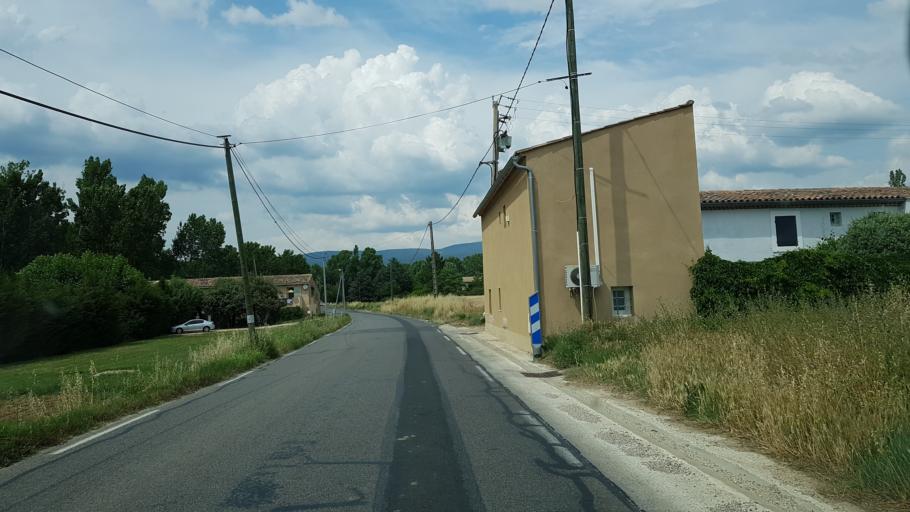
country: FR
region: Provence-Alpes-Cote d'Azur
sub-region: Departement du Vaucluse
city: Apt
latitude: 43.8962
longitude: 5.3832
